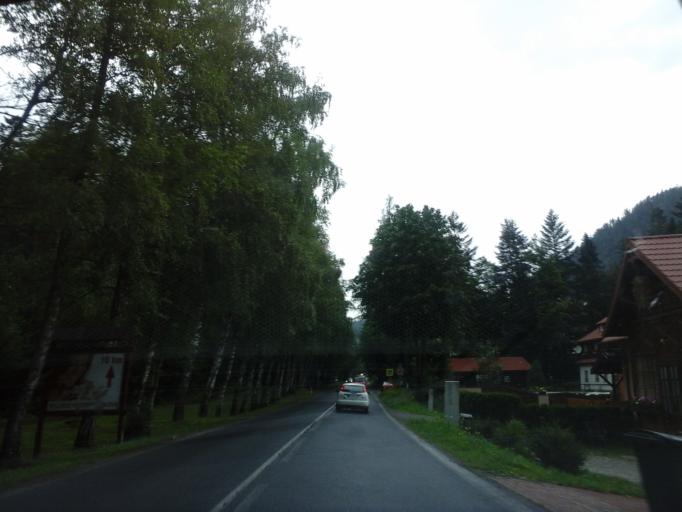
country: SK
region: Presovsky
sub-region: Okres Poprad
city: Zdiar
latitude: 49.2256
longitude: 20.3232
